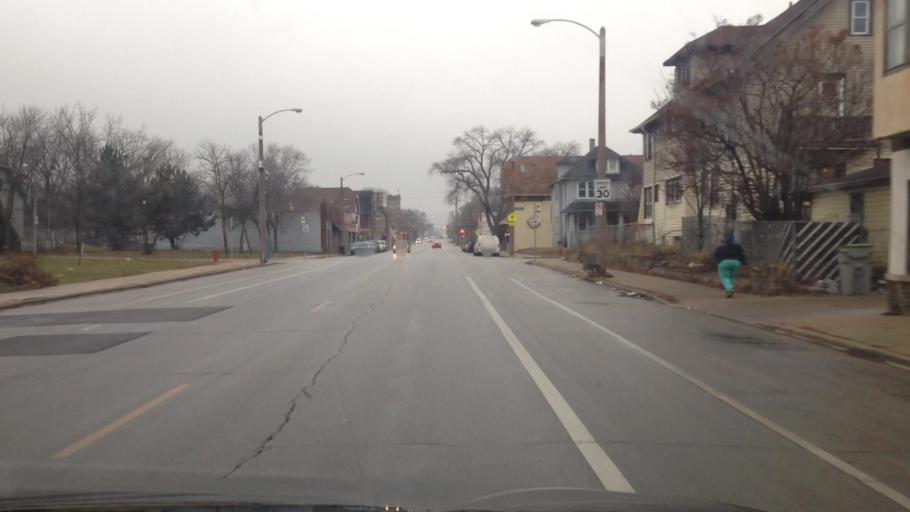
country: US
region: Wisconsin
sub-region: Milwaukee County
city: Wauwatosa
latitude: 43.0679
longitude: -87.9590
